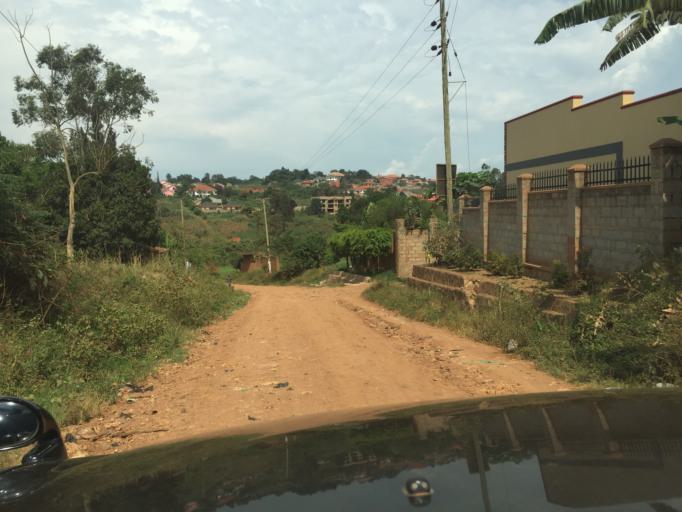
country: UG
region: Central Region
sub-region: Wakiso District
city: Kireka
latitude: 0.4133
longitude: 32.6251
